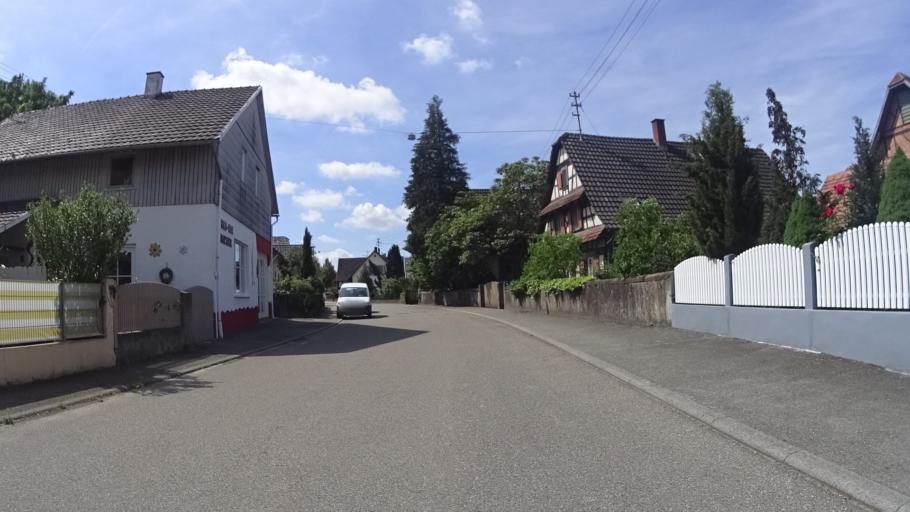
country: DE
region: Baden-Wuerttemberg
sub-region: Freiburg Region
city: Meissenheim
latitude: 48.4338
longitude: 7.8053
